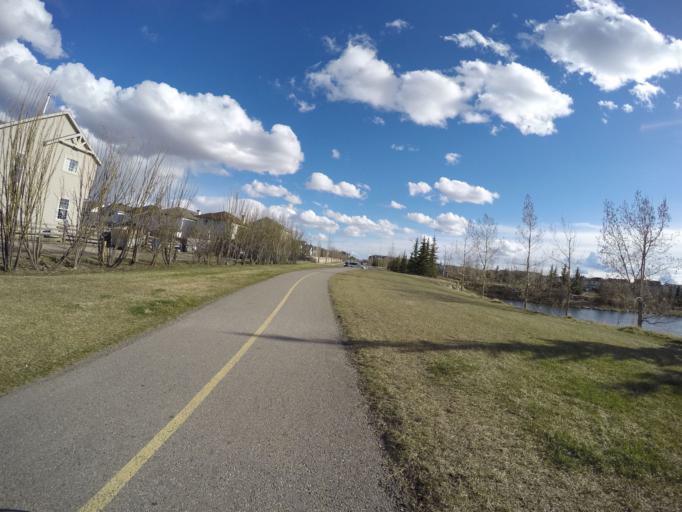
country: CA
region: Alberta
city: Calgary
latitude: 50.9110
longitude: -114.1172
